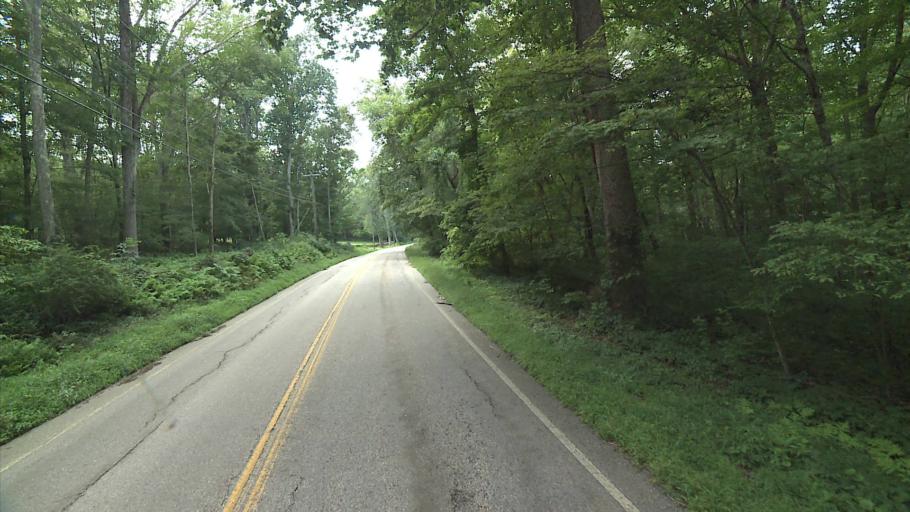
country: US
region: Connecticut
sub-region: Middlesex County
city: Essex Village
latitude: 41.4309
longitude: -72.3553
